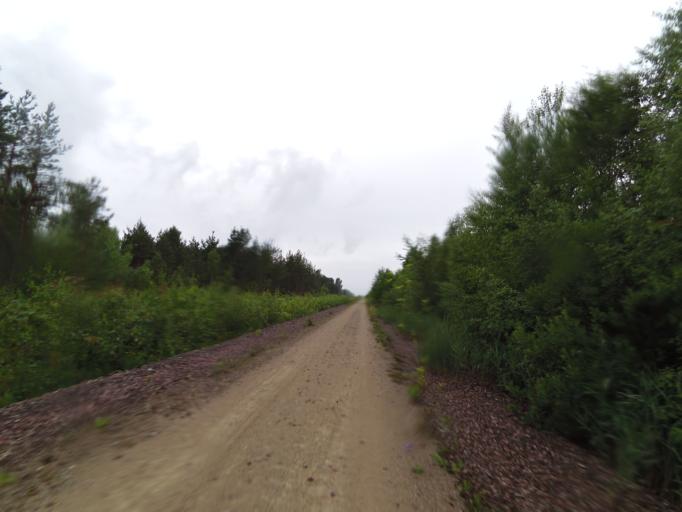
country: EE
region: Laeaene
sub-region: Ridala Parish
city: Uuemoisa
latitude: 58.9557
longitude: 23.8406
